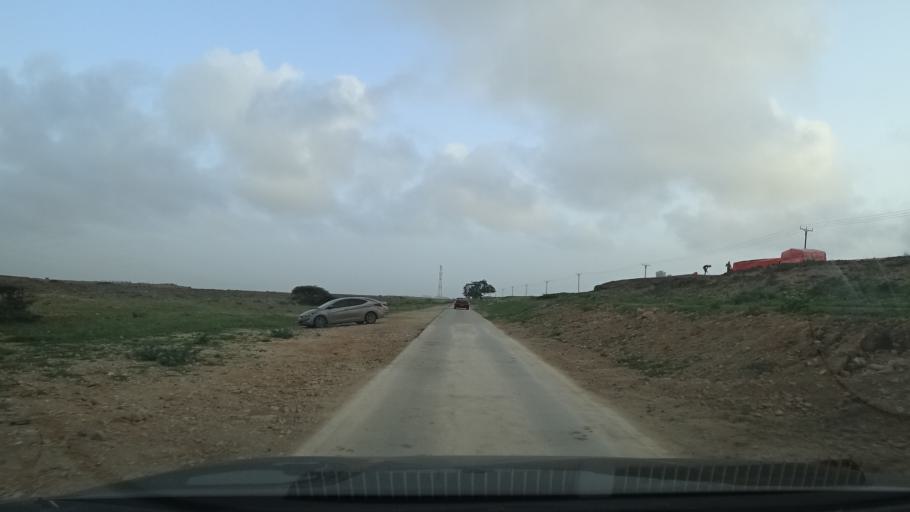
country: OM
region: Zufar
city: Salalah
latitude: 17.0924
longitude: 54.2331
